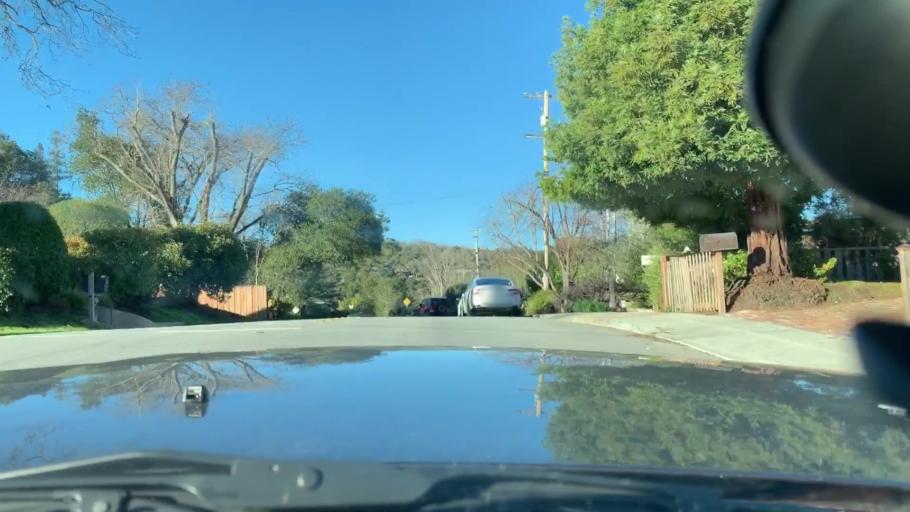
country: US
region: California
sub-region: San Mateo County
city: Ladera
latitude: 37.4025
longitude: -122.2011
